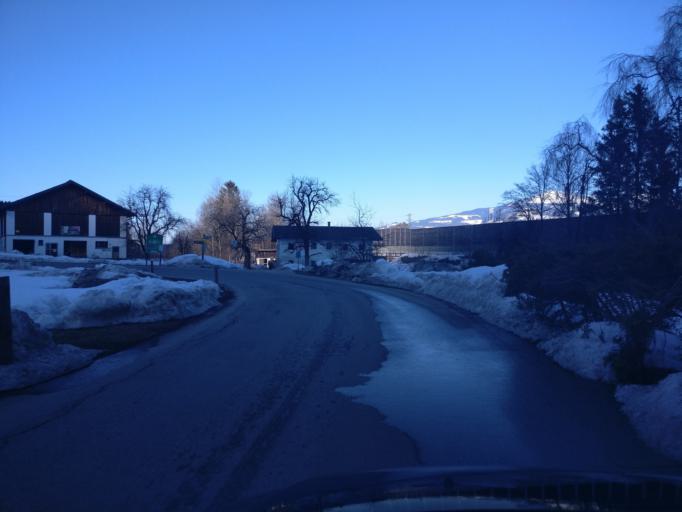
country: AT
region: Salzburg
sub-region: Politischer Bezirk Hallein
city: Golling an der Salzach
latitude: 47.6018
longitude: 13.1487
